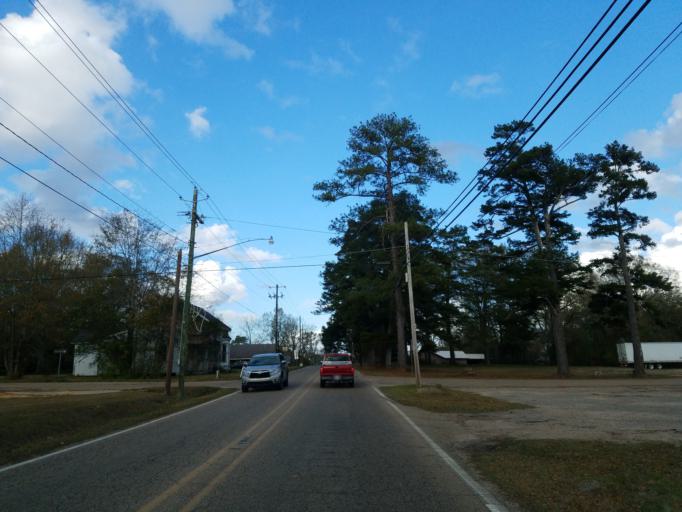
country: US
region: Mississippi
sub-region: Jones County
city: Ellisville
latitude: 31.5983
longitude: -89.1975
